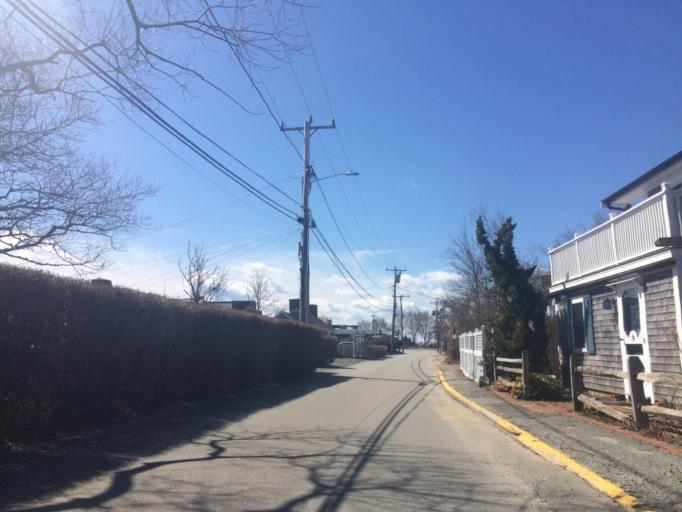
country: US
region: Massachusetts
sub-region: Barnstable County
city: Provincetown
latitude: 42.0390
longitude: -70.1954
